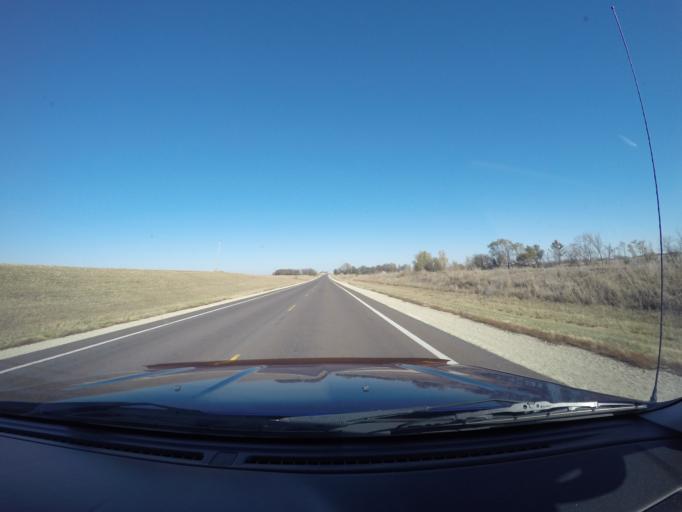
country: US
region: Kansas
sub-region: Marshall County
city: Blue Rapids
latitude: 39.6210
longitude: -96.7502
